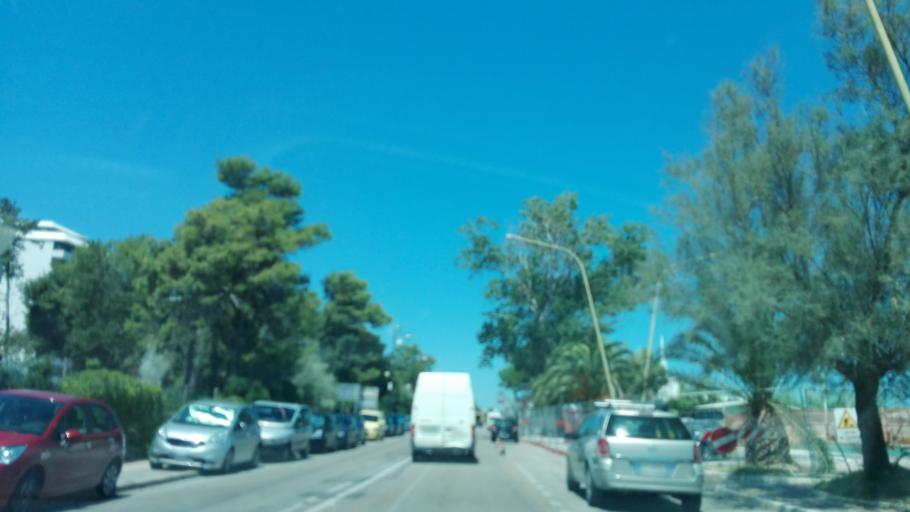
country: IT
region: Abruzzo
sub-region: Provincia di Pescara
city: Villa Raspa
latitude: 42.4932
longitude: 14.1855
